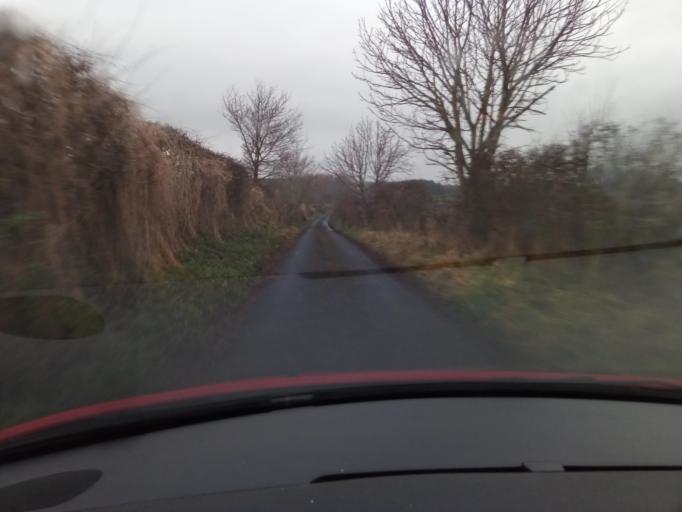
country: GB
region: Scotland
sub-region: The Scottish Borders
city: Kelso
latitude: 55.5292
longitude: -2.4643
